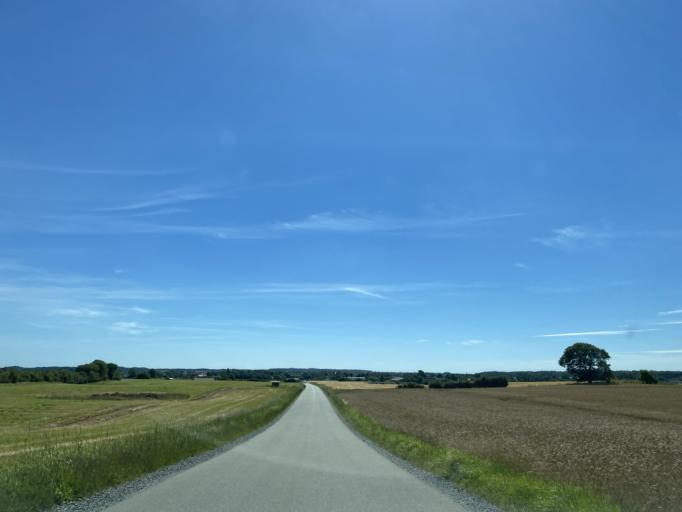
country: DK
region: South Denmark
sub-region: Vejle Kommune
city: Vejle
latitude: 55.6284
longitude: 9.5387
